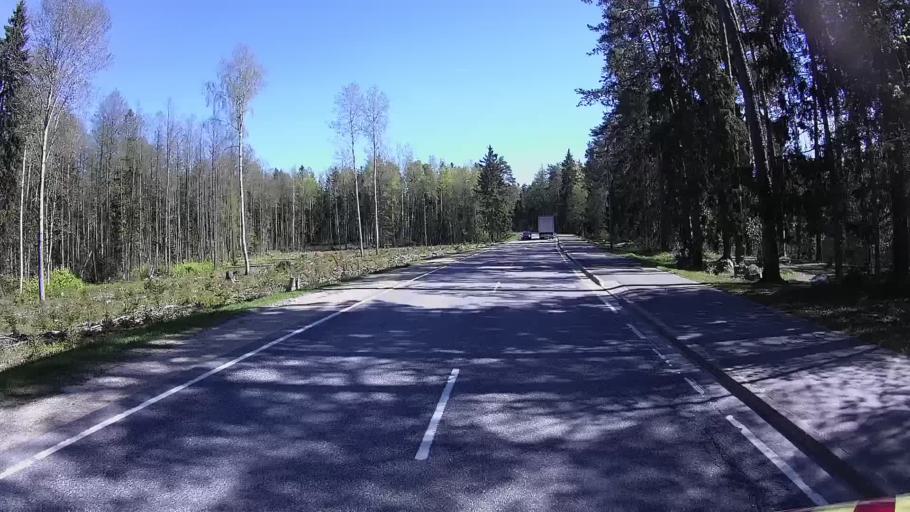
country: EE
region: Harju
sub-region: Kuusalu vald
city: Kuusalu
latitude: 59.2733
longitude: 25.6324
